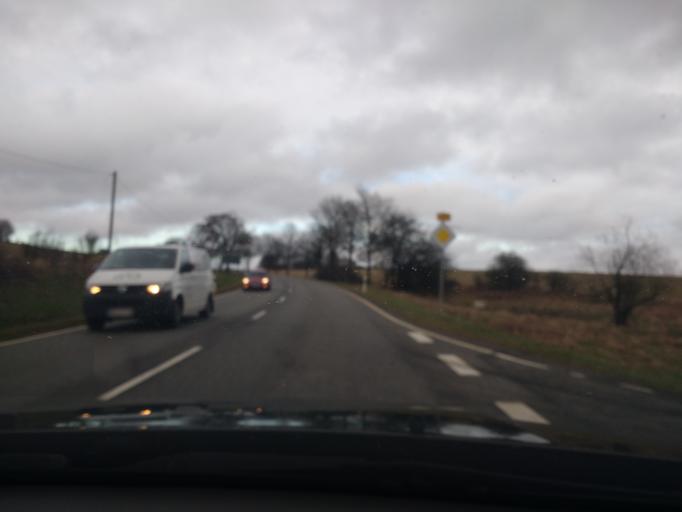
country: DE
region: Rheinland-Pfalz
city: Kell
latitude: 49.6360
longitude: 6.8375
